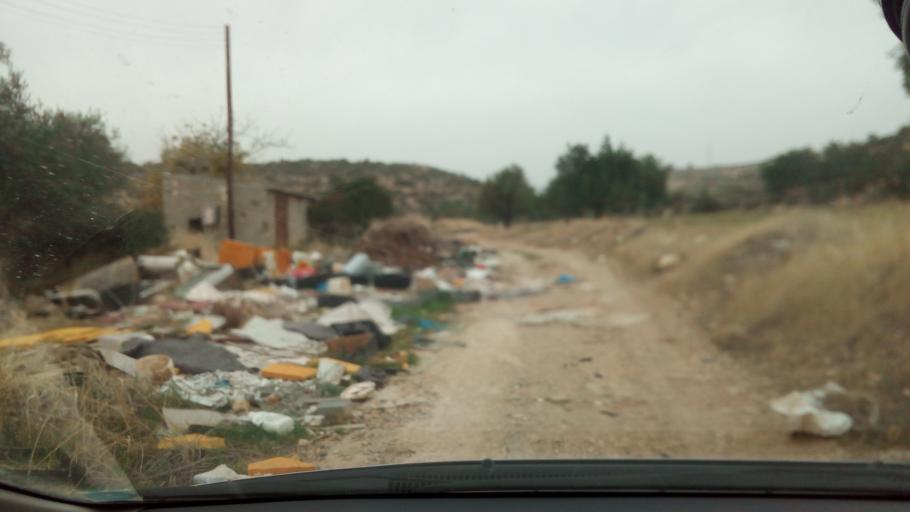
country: CY
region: Limassol
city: Ypsonas
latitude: 34.7099
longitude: 32.9559
